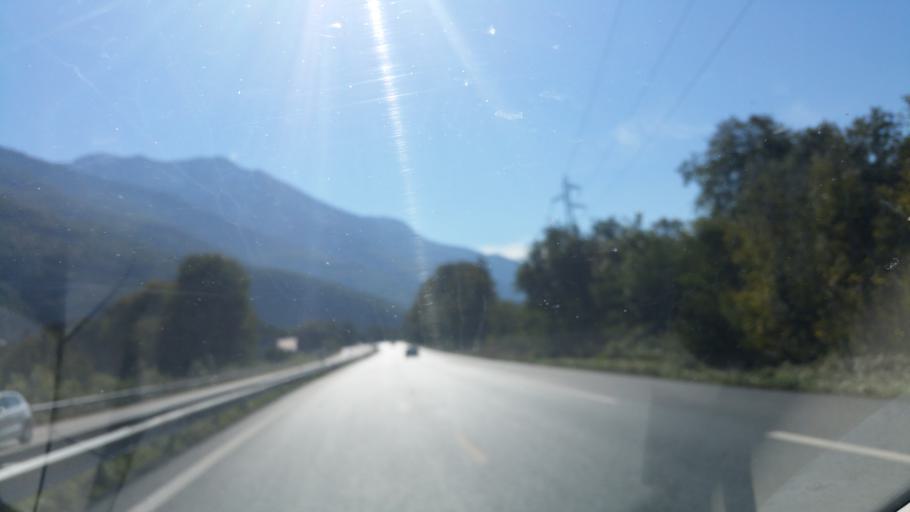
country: FR
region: Rhone-Alpes
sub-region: Departement de la Savoie
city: La Bathie
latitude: 45.6561
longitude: 6.4322
